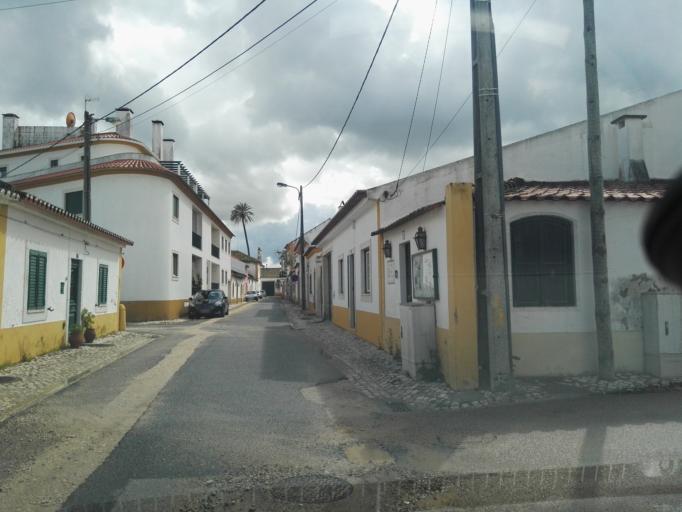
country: PT
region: Santarem
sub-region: Golega
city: Golega
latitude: 39.4042
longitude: -8.4848
